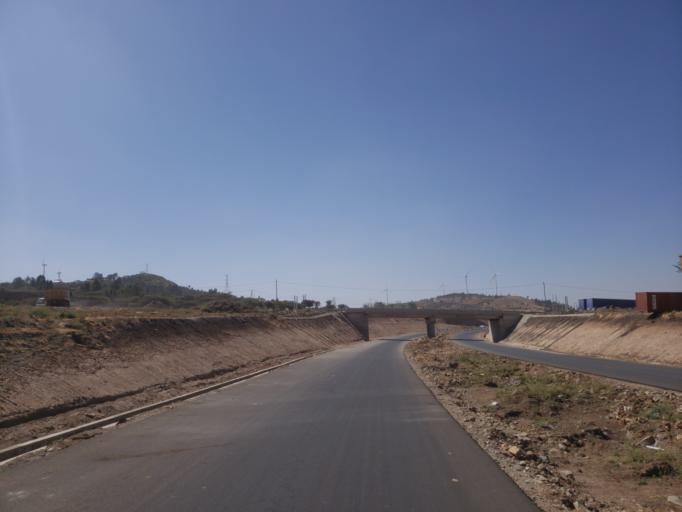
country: ET
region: Oromiya
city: Mojo
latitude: 8.5688
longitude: 39.1658
